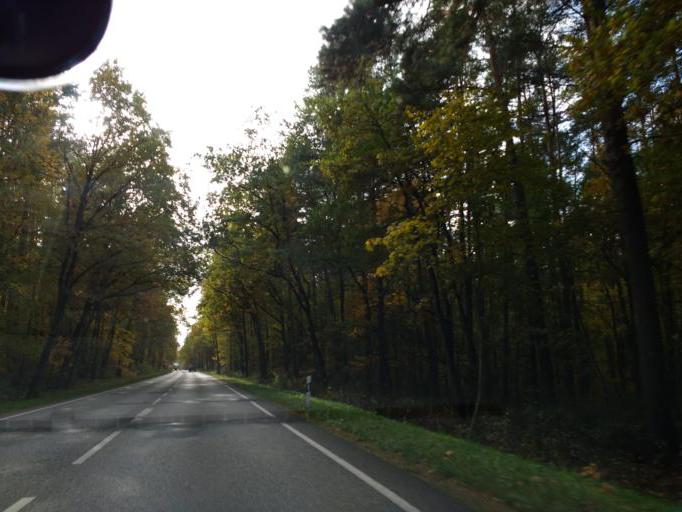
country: DE
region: Brandenburg
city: Petershagen
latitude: 52.5221
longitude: 13.8124
